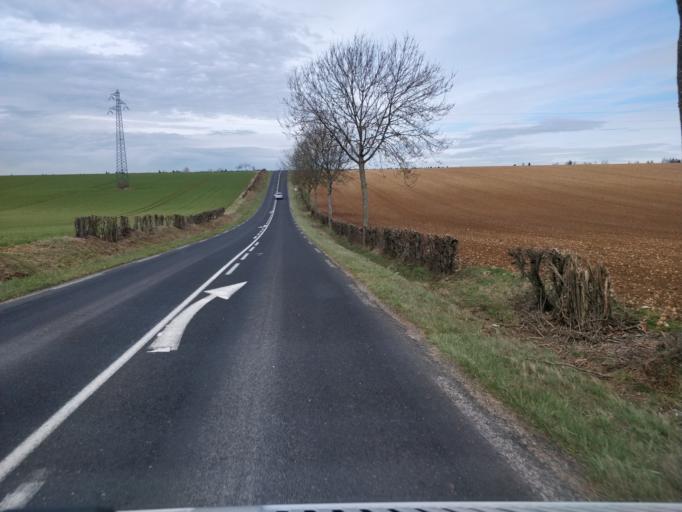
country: FR
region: Lorraine
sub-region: Departement de Meurthe-et-Moselle
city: Montauville
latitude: 48.9067
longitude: 5.9428
